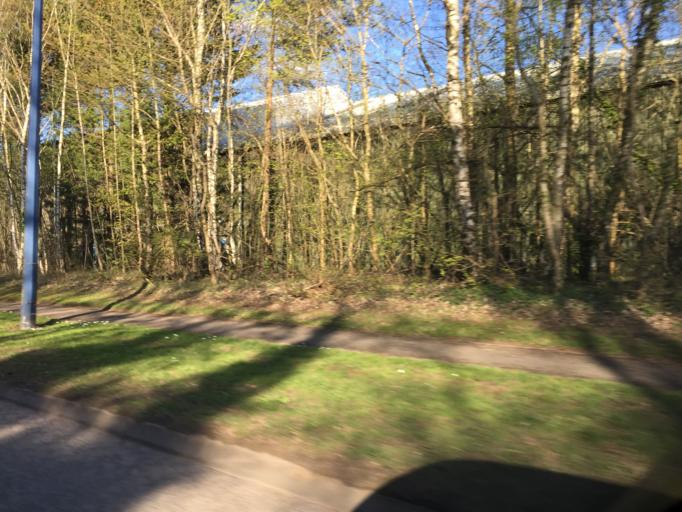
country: GB
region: Wales
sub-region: Torfaen County Borough
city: Cwmbran
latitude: 51.6626
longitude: -3.0232
